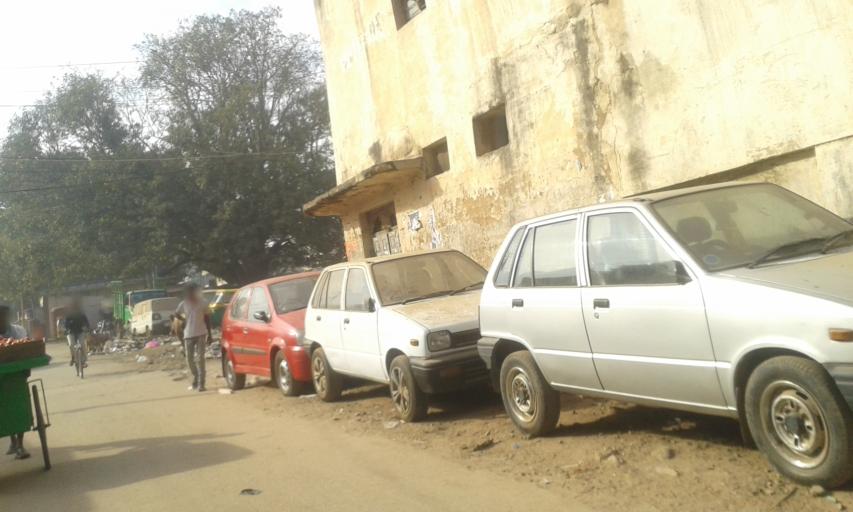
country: IN
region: Karnataka
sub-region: Bangalore Urban
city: Bangalore
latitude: 12.9592
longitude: 77.6185
